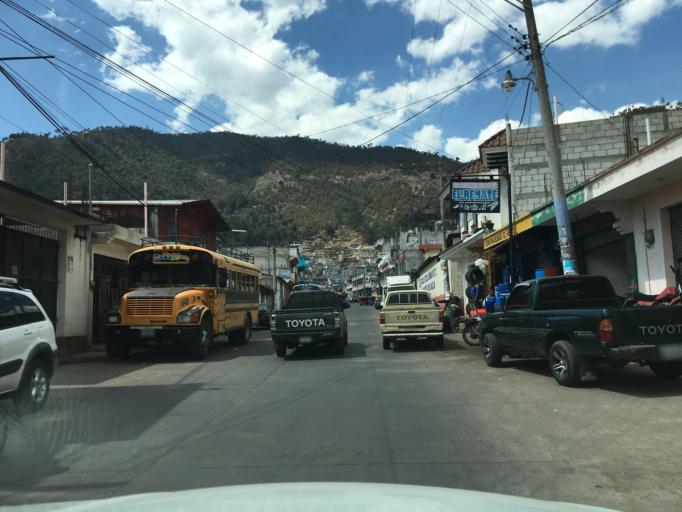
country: GT
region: Totonicapan
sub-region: Municipio de San Andres Xecul
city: San Andres Xecul
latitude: 14.9050
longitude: -91.4791
